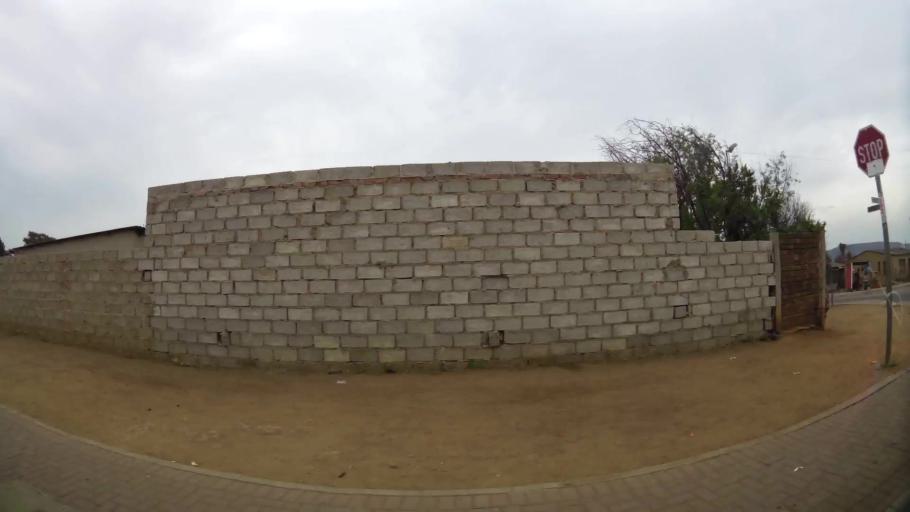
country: ZA
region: Gauteng
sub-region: City of Tshwane Metropolitan Municipality
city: Pretoria
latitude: -25.7125
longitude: 28.3421
